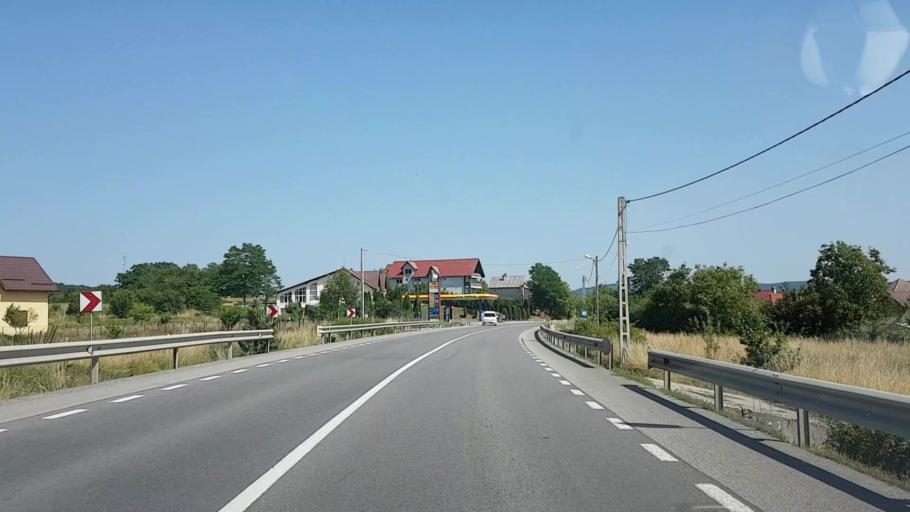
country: RO
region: Bistrita-Nasaud
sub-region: Comuna Uriu
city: Cristestii Ciceului
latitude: 47.1818
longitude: 24.1379
